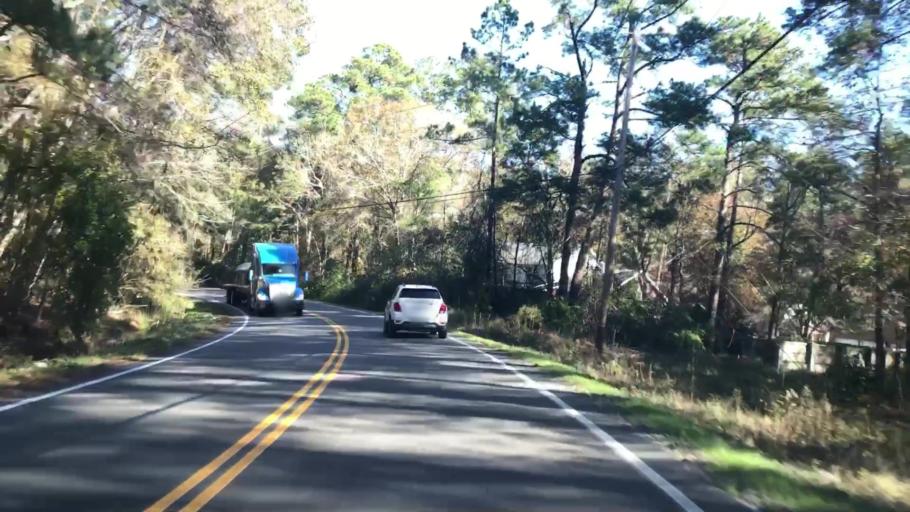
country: US
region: South Carolina
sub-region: Dorchester County
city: Summerville
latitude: 33.0237
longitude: -80.1956
